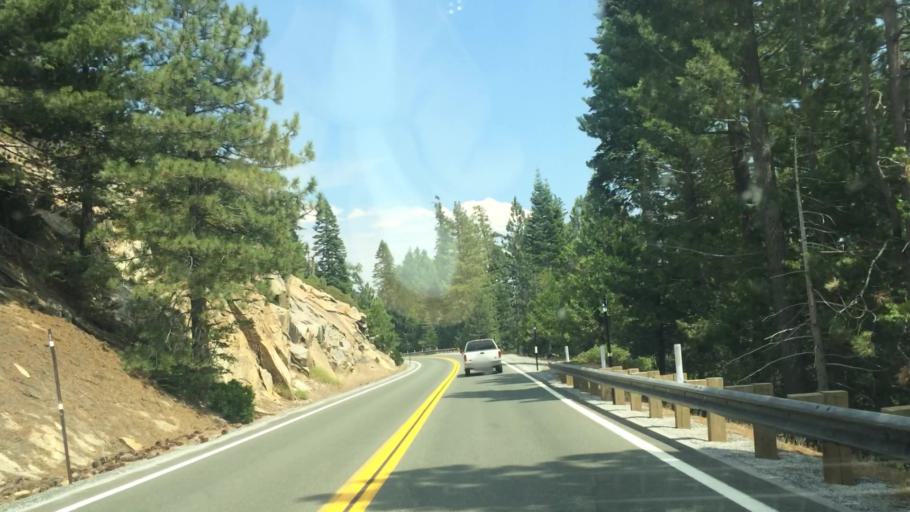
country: US
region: California
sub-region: Amador County
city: Pioneer
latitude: 38.5450
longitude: -120.3340
